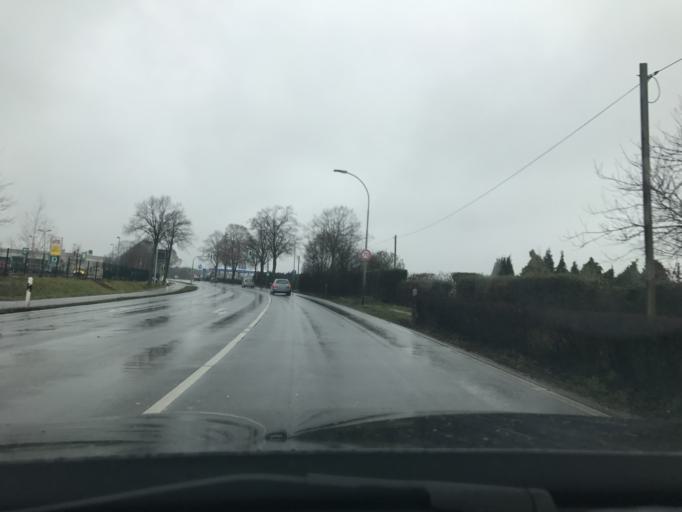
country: DE
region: North Rhine-Westphalia
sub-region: Regierungsbezirk Dusseldorf
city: Rheurdt
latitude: 51.4421
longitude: 6.4179
